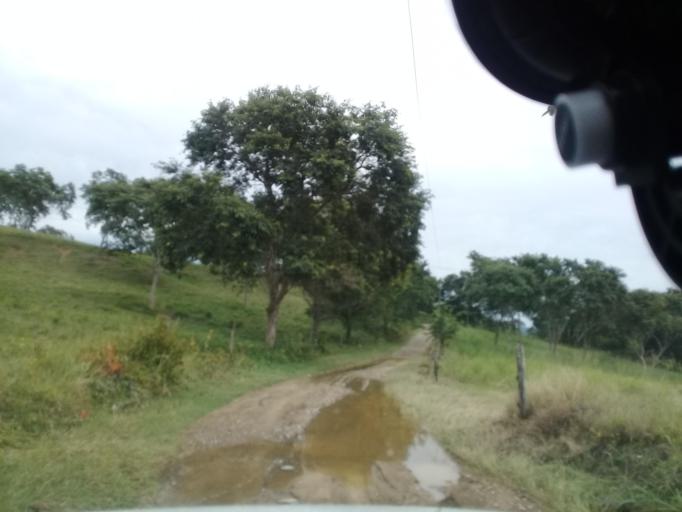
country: MX
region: Hidalgo
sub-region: Huejutla de Reyes
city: Parque de Poblamiento Solidaridad
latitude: 21.1783
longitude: -98.3788
